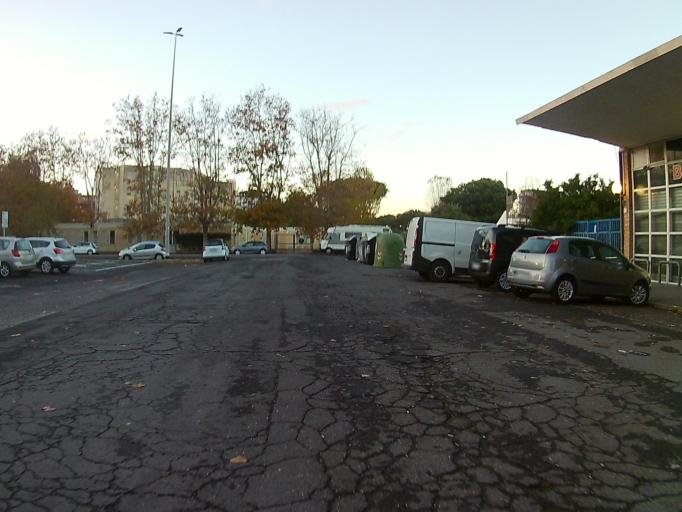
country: IT
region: Latium
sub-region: Citta metropolitana di Roma Capitale
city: Lido di Ostia
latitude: 41.7269
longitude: 12.2950
